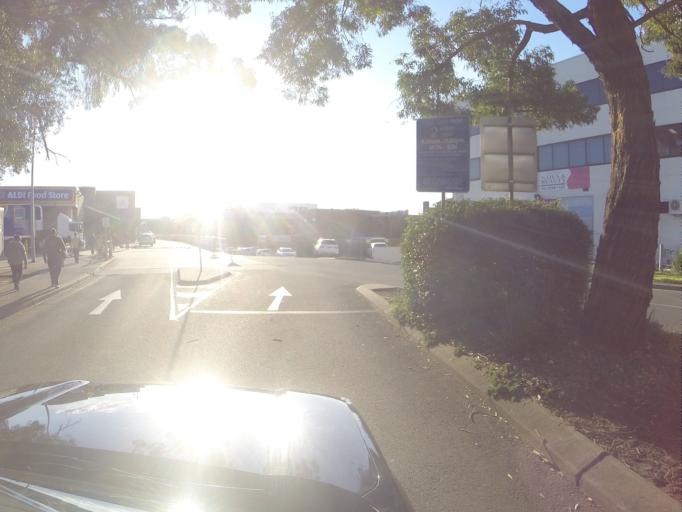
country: AU
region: New South Wales
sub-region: Ashfield
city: Ashfield
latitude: -33.8900
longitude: 151.1255
